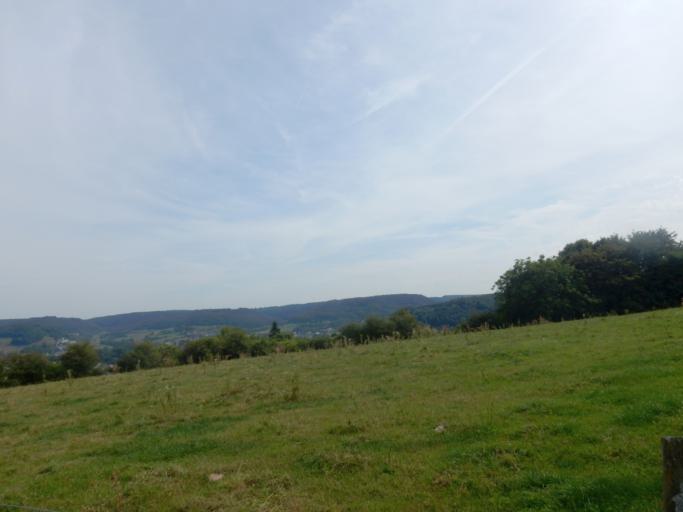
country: LU
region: Luxembourg
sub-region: Canton de Mersch
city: Mersch
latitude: 49.7414
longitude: 6.0859
